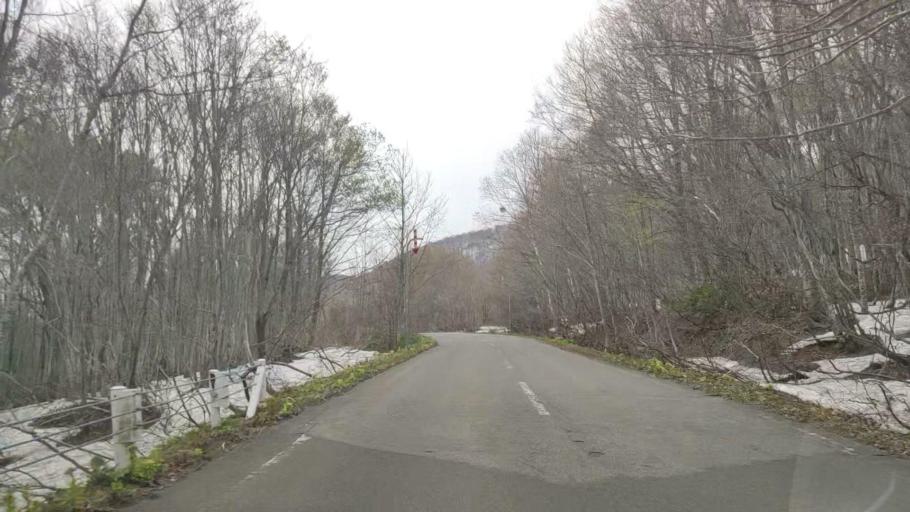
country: JP
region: Aomori
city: Aomori Shi
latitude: 40.6597
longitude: 140.9620
